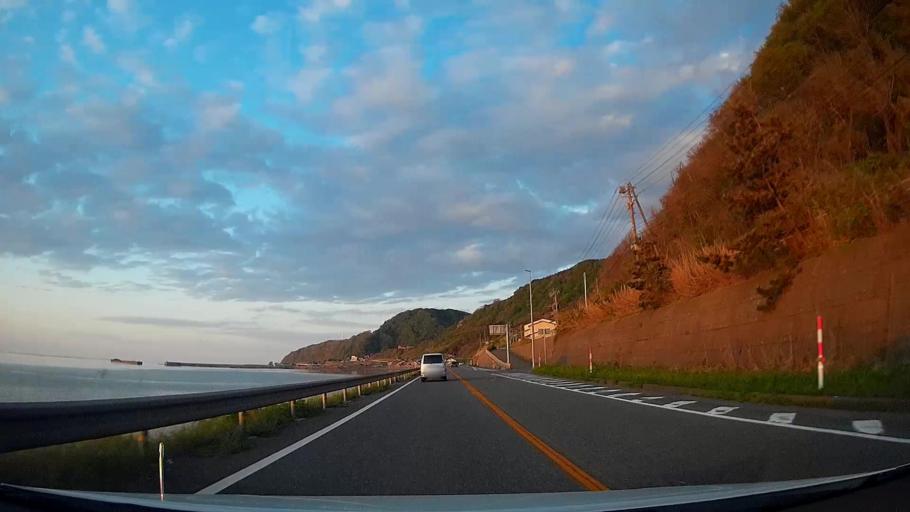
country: JP
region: Niigata
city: Joetsu
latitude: 37.1249
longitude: 138.0428
